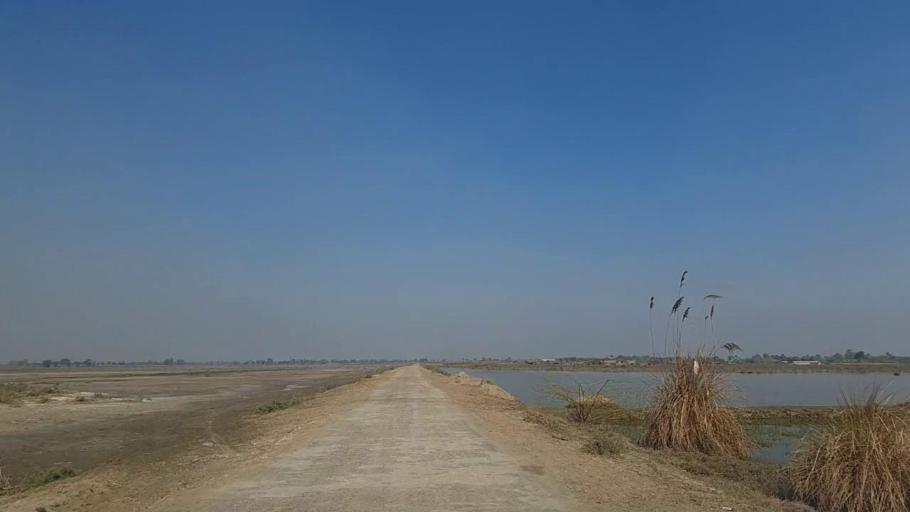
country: PK
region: Sindh
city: Daur
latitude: 26.4715
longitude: 68.3252
